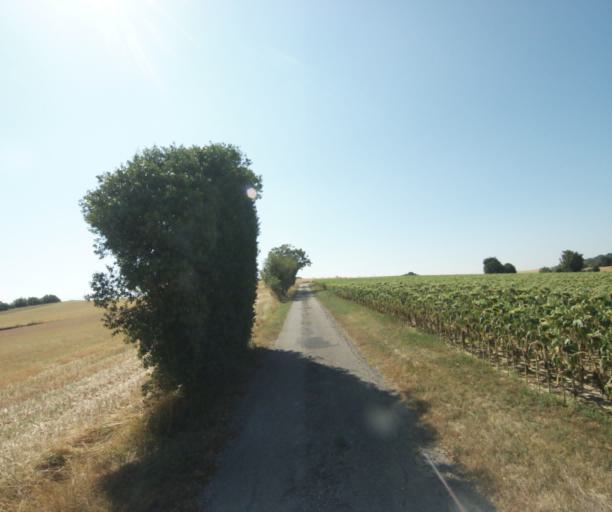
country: FR
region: Midi-Pyrenees
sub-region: Departement de la Haute-Garonne
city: Saint-Felix-Lauragais
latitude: 43.5178
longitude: 1.9393
